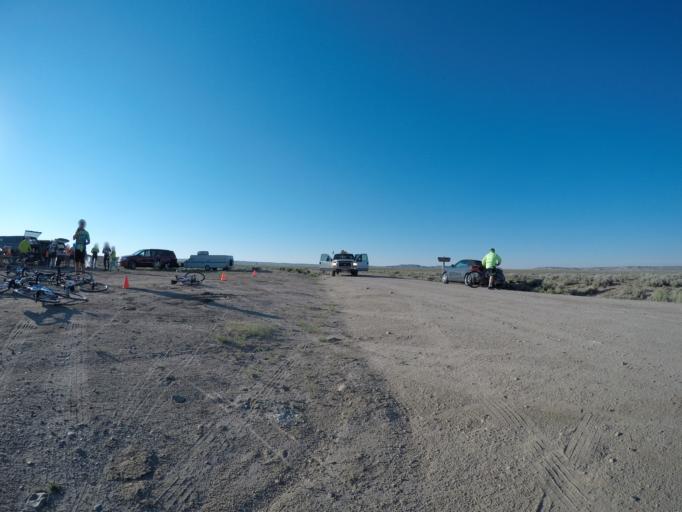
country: US
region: Wyoming
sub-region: Sublette County
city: Pinedale
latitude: 42.6018
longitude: -109.8353
